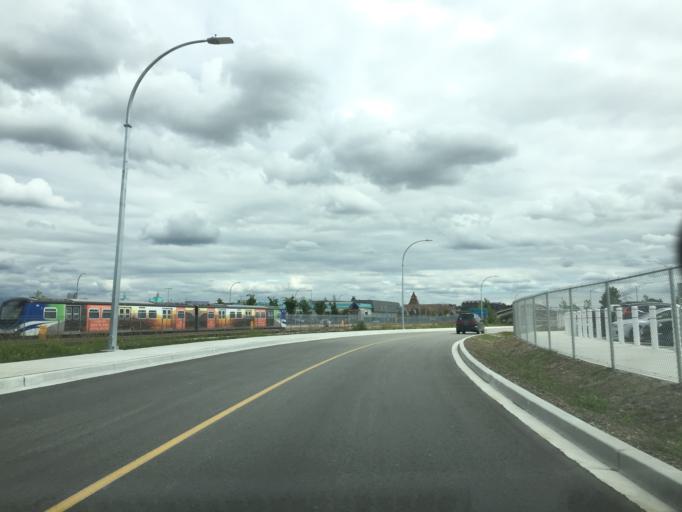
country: CA
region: British Columbia
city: Richmond
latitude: 49.1965
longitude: -123.1453
